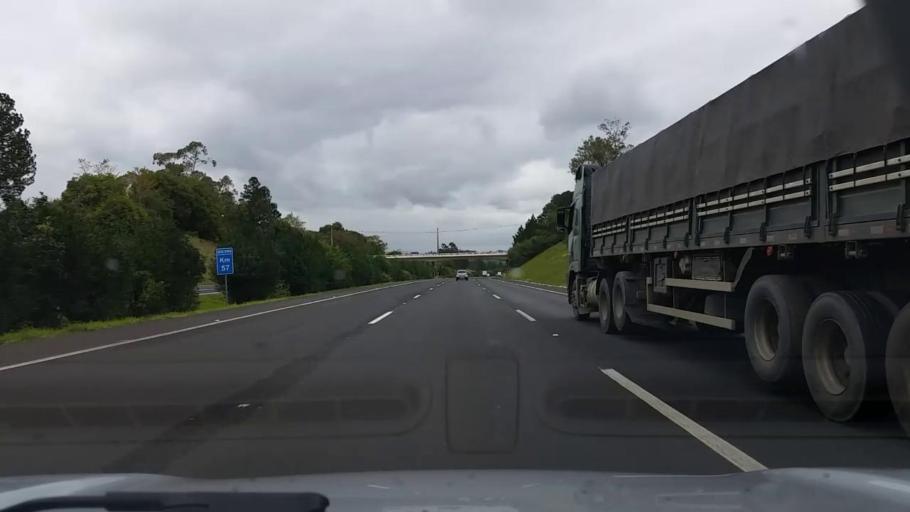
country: BR
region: Rio Grande do Sul
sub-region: Gravatai
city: Gravatai
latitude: -29.9186
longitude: -50.8280
